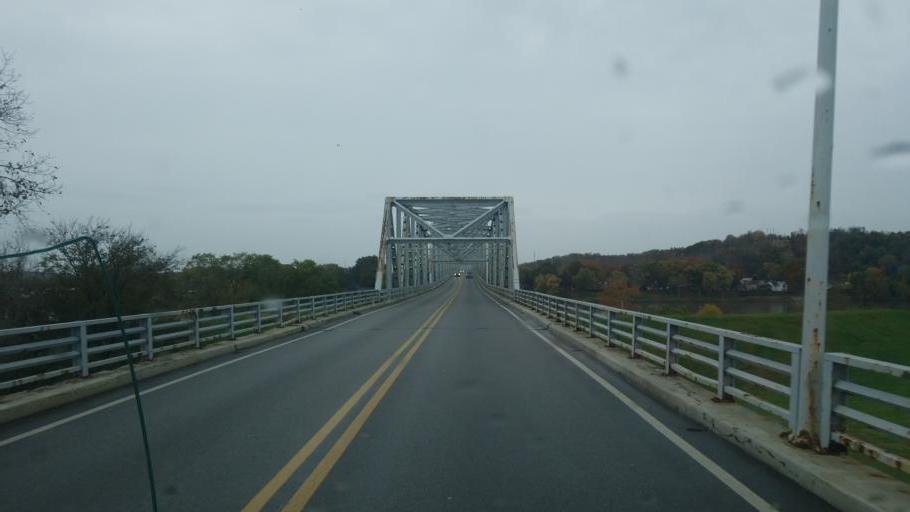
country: US
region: West Virginia
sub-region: Wood County
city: Parkersburg
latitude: 39.2831
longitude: -81.5590
